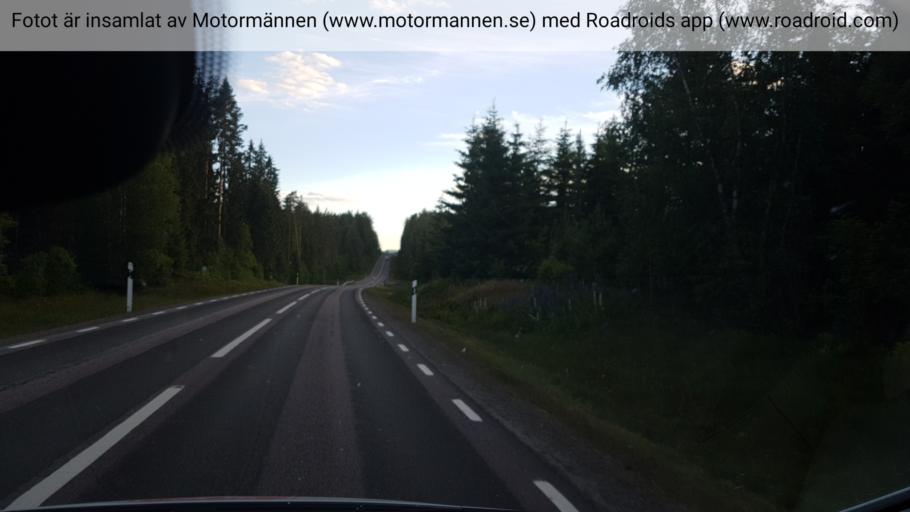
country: SE
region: Vaermland
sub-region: Torsby Kommun
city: Torsby
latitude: 60.3241
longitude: 13.1233
